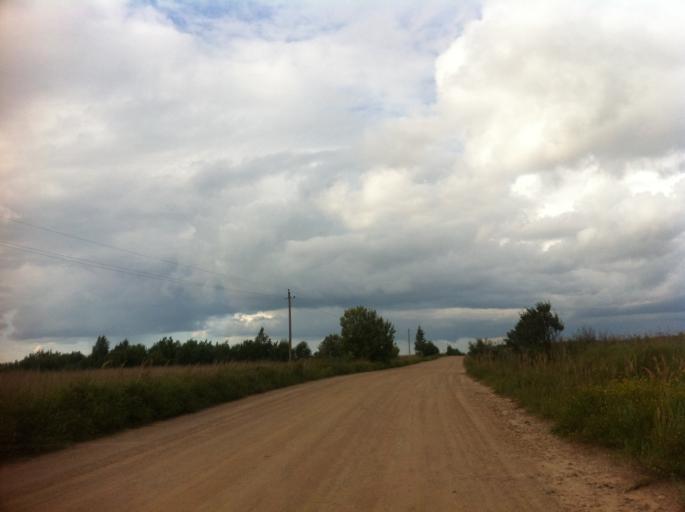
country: RU
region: Pskov
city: Izborsk
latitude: 57.8204
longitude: 27.9780
